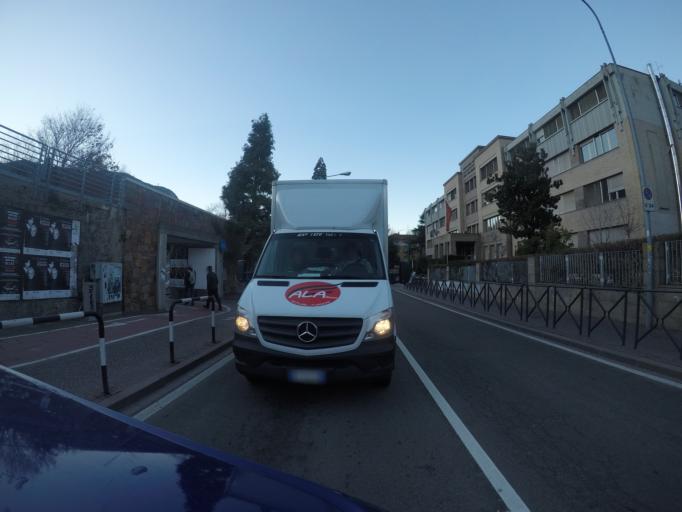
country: IT
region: Trentino-Alto Adige
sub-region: Bolzano
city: Bolzano
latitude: 46.5043
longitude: 11.3464
